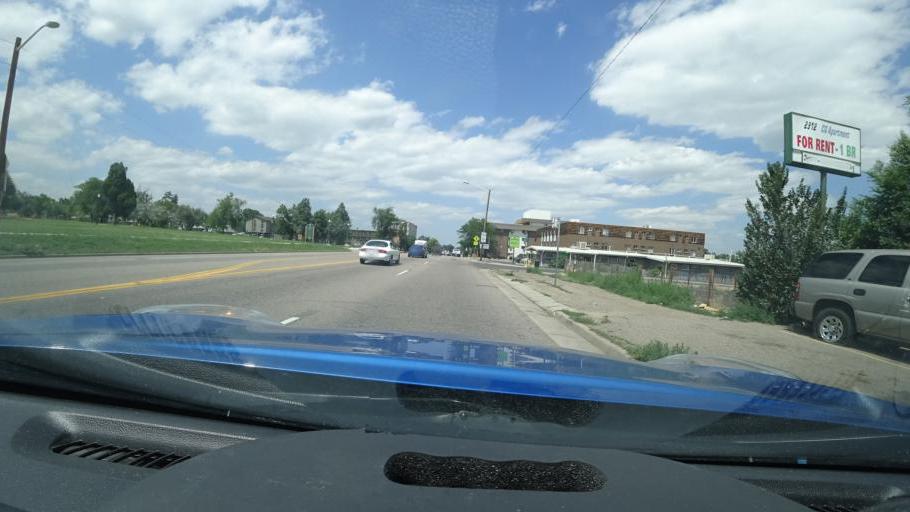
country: US
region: Colorado
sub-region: Arapahoe County
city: Sheridan
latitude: 39.6634
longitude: -105.0250
